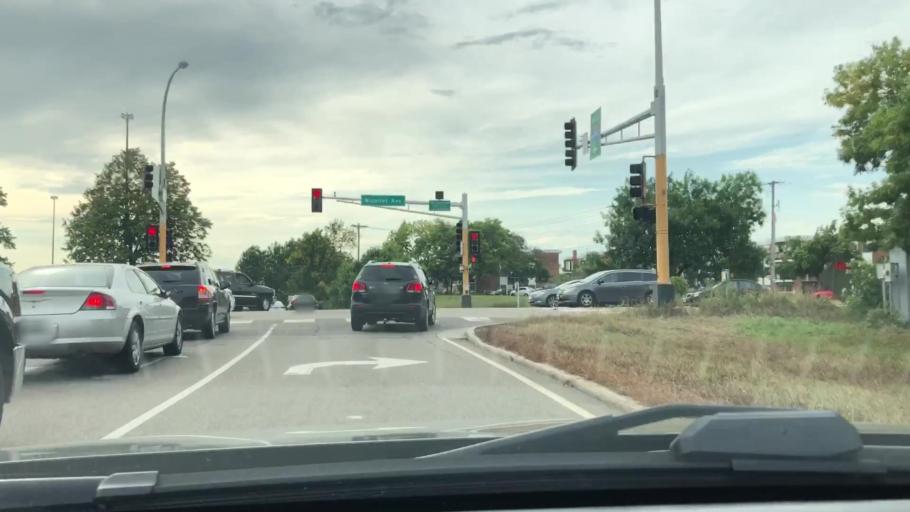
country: US
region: Minnesota
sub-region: Hennepin County
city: Richfield
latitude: 44.8623
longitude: -93.2778
